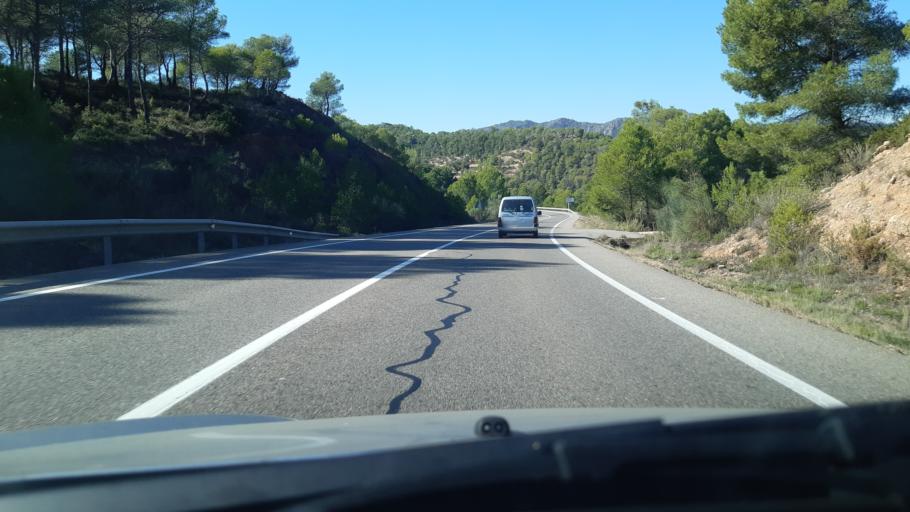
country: ES
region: Catalonia
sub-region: Provincia de Tarragona
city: Rasquera
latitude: 41.0069
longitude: 0.6021
